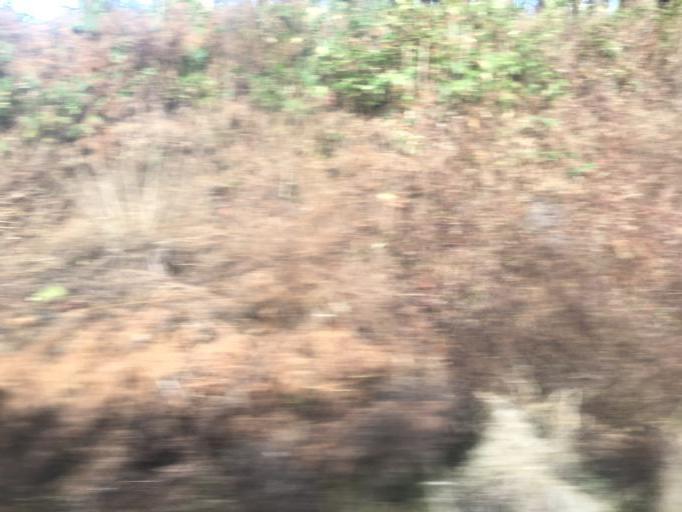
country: JP
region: Akita
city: Odate
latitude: 40.2712
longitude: 140.4577
